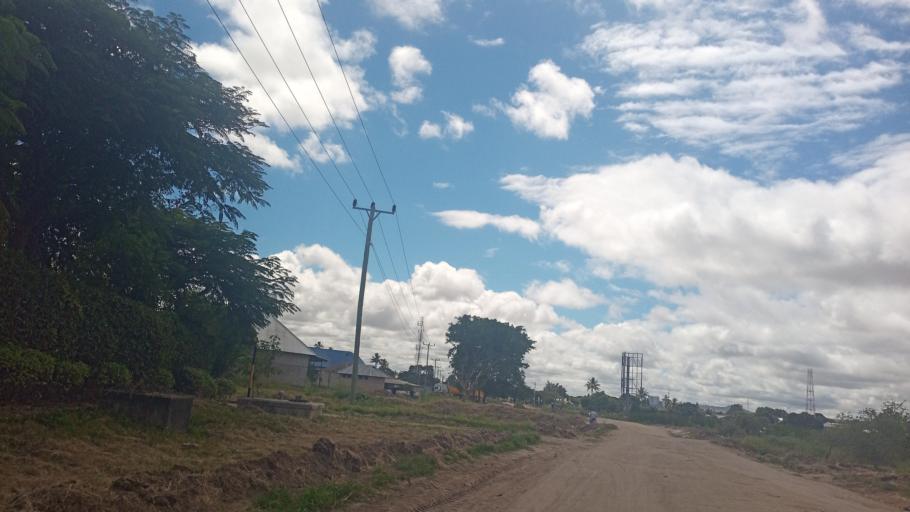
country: TZ
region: Dodoma
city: Dodoma
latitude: -6.1881
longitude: 35.7314
